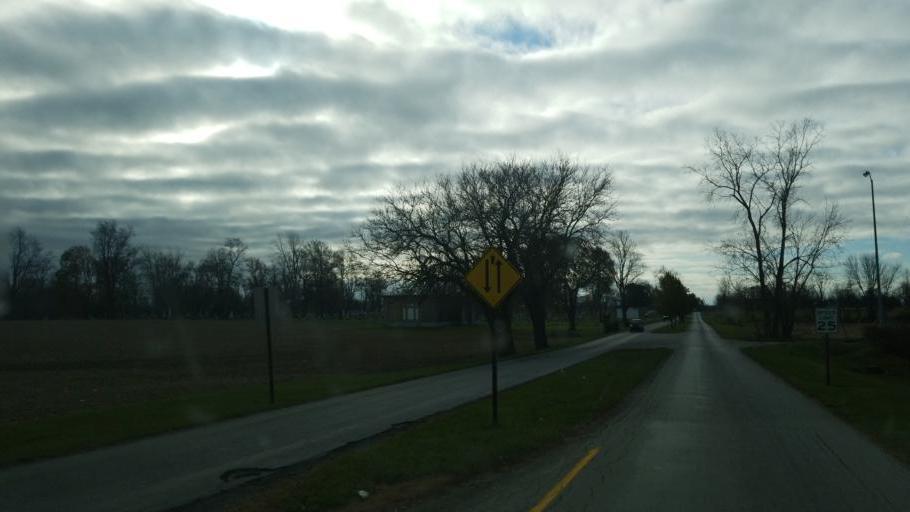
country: US
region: Ohio
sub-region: Hardin County
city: Kenton
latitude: 40.6504
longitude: -83.5905
